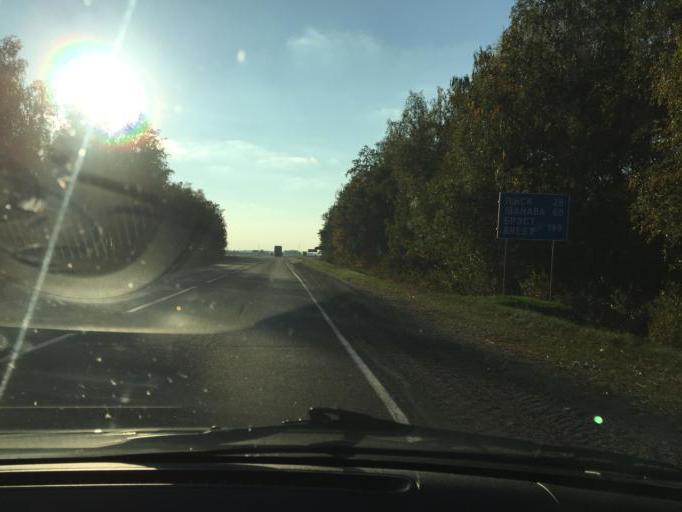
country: BY
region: Brest
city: Asnyezhytsy
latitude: 52.2740
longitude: 26.3835
